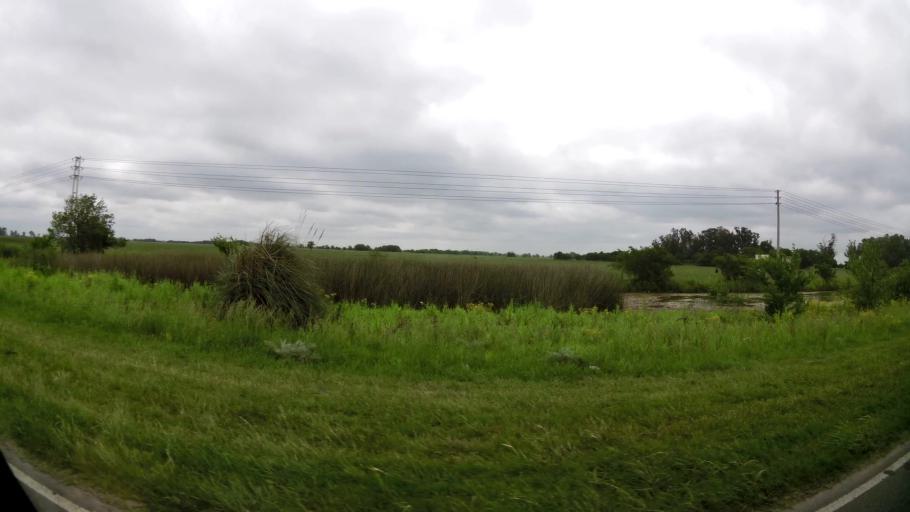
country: AR
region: Buenos Aires
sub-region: Partido de San Vicente
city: San Vicente
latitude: -34.9876
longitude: -58.4682
